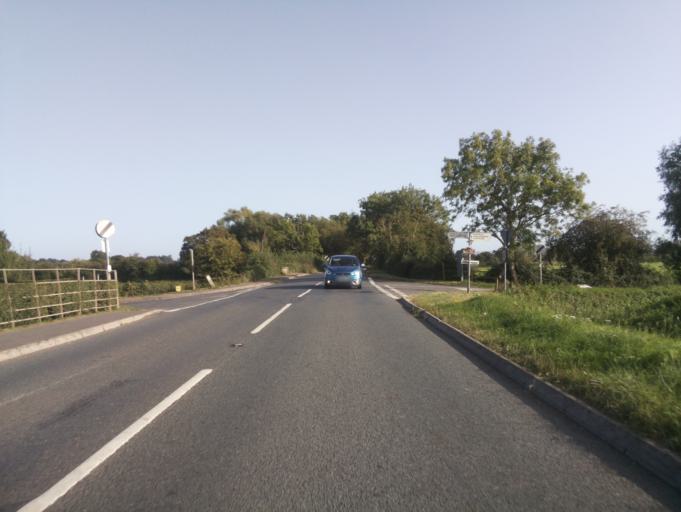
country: GB
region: England
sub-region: Gloucestershire
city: Tewkesbury
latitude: 51.9535
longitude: -2.2363
